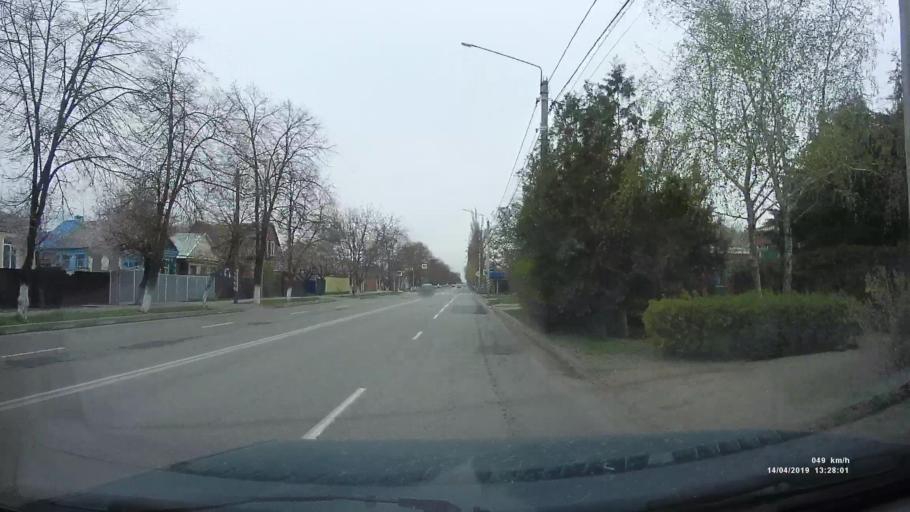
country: RU
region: Rostov
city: Azov
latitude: 47.0952
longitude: 39.4470
